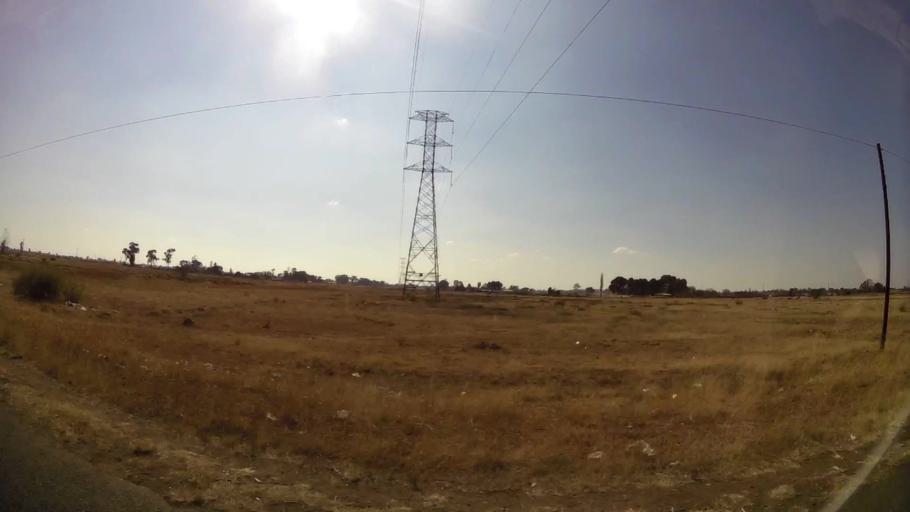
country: ZA
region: Orange Free State
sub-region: Mangaung Metropolitan Municipality
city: Bloemfontein
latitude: -29.1756
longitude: 26.3041
